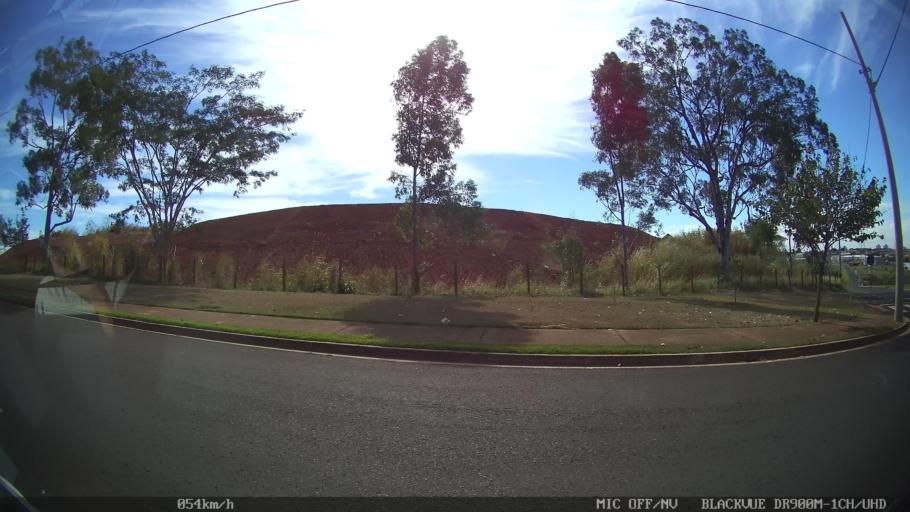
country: BR
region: Sao Paulo
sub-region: Sao Jose Do Rio Preto
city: Sao Jose do Rio Preto
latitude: -20.8504
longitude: -49.3751
